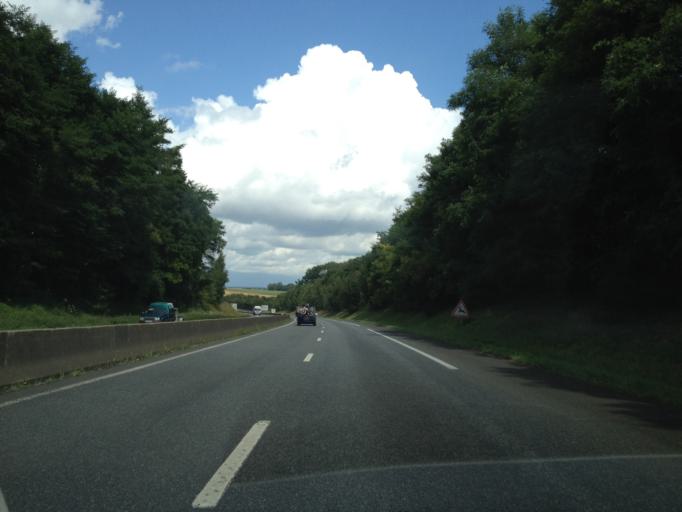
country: FR
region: Picardie
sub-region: Departement de la Somme
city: Abbeville
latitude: 50.0642
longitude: 1.7897
